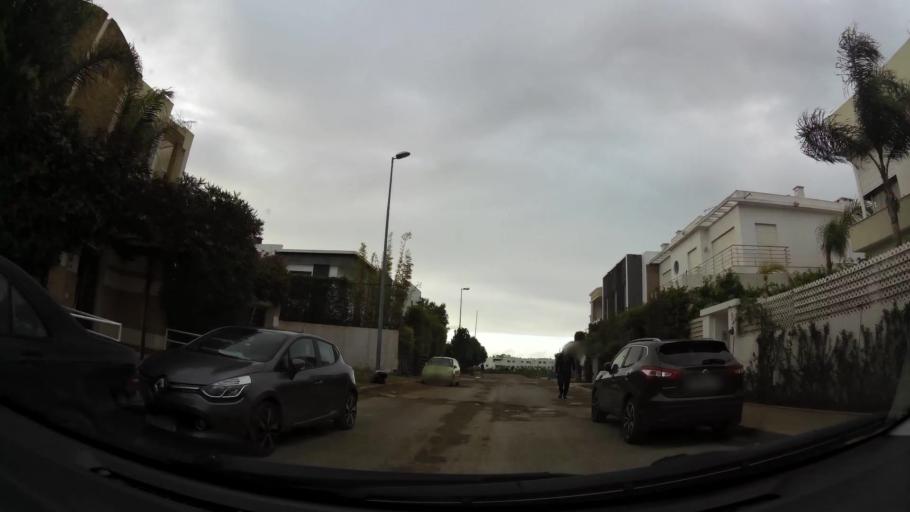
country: MA
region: Grand Casablanca
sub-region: Casablanca
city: Casablanca
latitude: 33.5768
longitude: -7.6802
